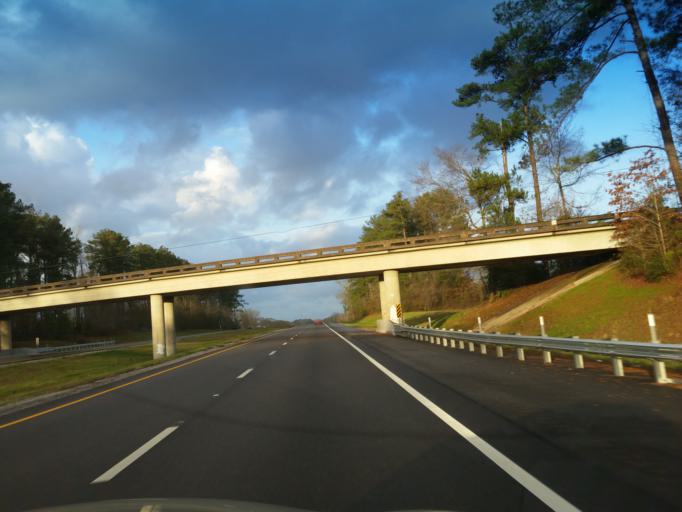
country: US
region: Mississippi
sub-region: Jones County
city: Sharon
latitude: 31.9303
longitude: -88.9981
